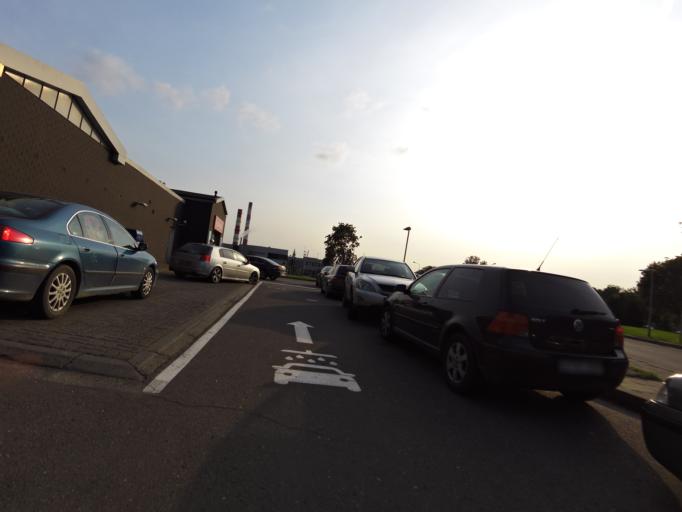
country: LT
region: Vilnius County
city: Vilkpede
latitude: 54.6711
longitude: 25.2365
